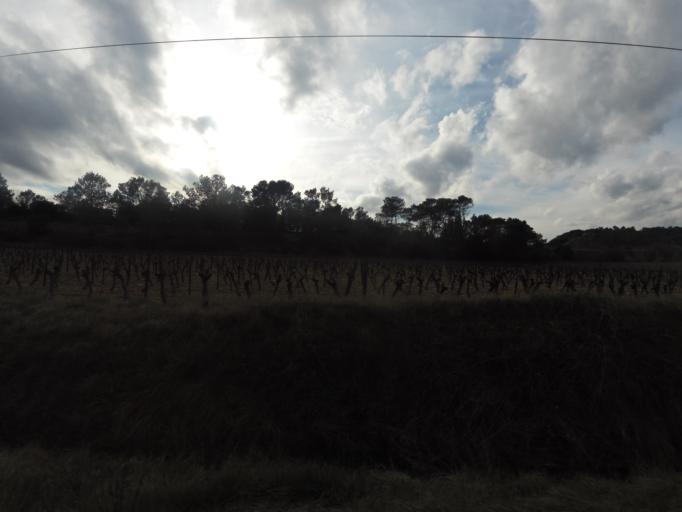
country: FR
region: Languedoc-Roussillon
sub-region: Departement du Gard
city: Saint-Mamert-du-Gard
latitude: 43.8927
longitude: 4.2298
